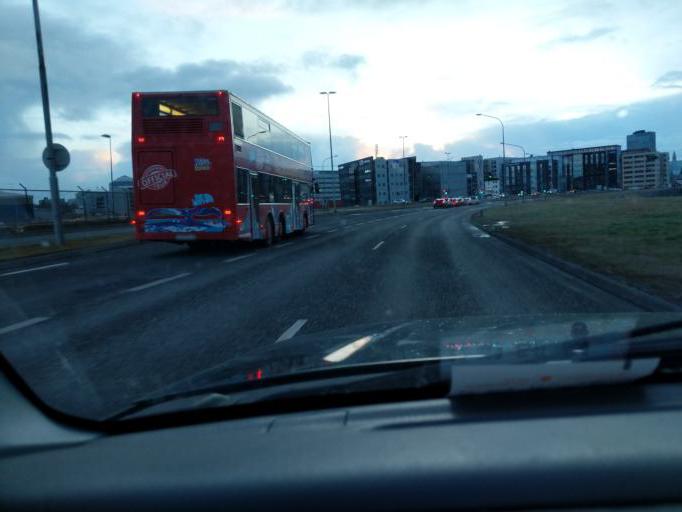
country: IS
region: Capital Region
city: Reykjavik
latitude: 64.1484
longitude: -21.8913
